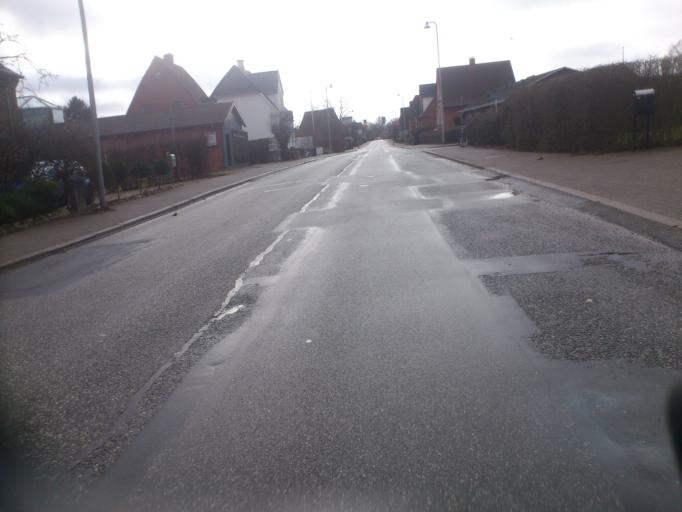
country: DK
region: South Denmark
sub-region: Fredericia Kommune
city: Fredericia
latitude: 55.5748
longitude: 9.7534
